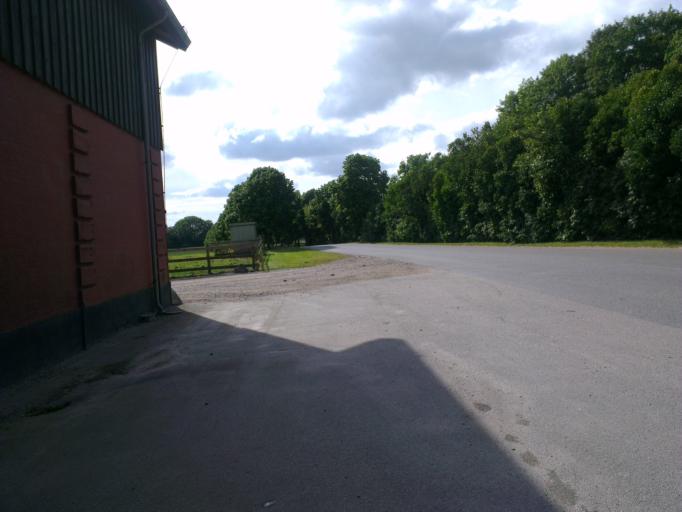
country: DK
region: Capital Region
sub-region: Frederikssund Kommune
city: Skibby
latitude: 55.7280
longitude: 11.9506
